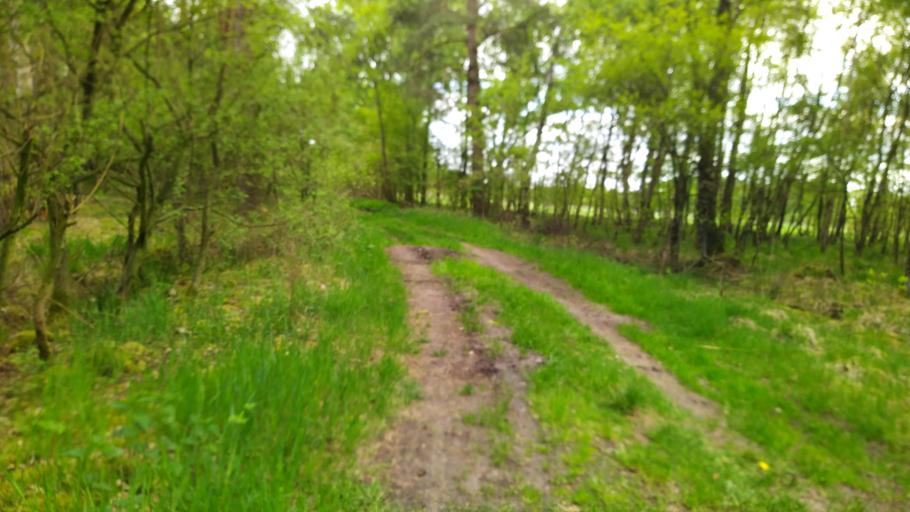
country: DE
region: Lower Saxony
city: Brest
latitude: 53.4306
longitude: 9.3905
